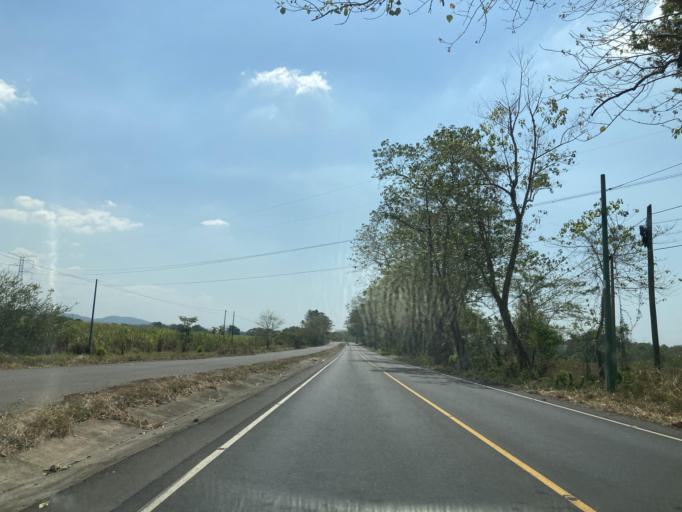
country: GT
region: Escuintla
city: Guanagazapa
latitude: 14.1971
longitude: -90.6987
